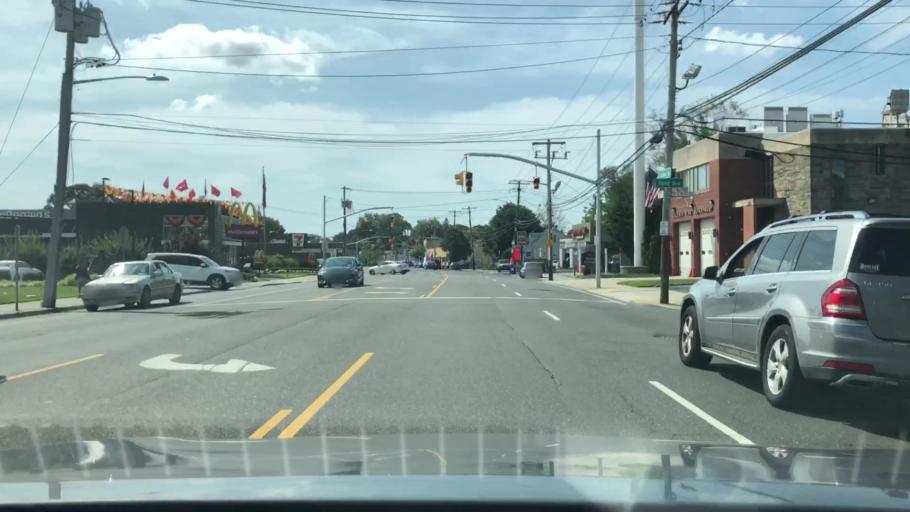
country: US
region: New York
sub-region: Nassau County
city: South Hempstead
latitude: 40.6803
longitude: -73.6150
